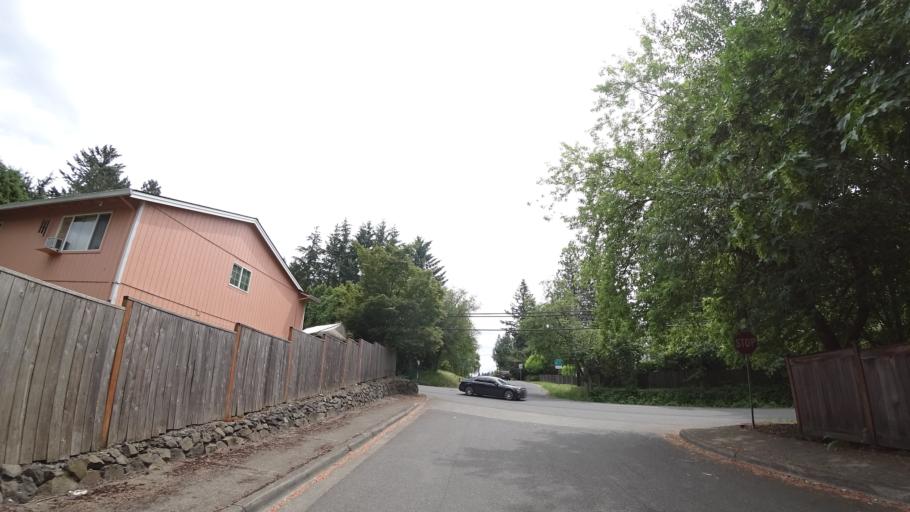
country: US
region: Oregon
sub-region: Washington County
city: Metzger
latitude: 45.4546
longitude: -122.7526
